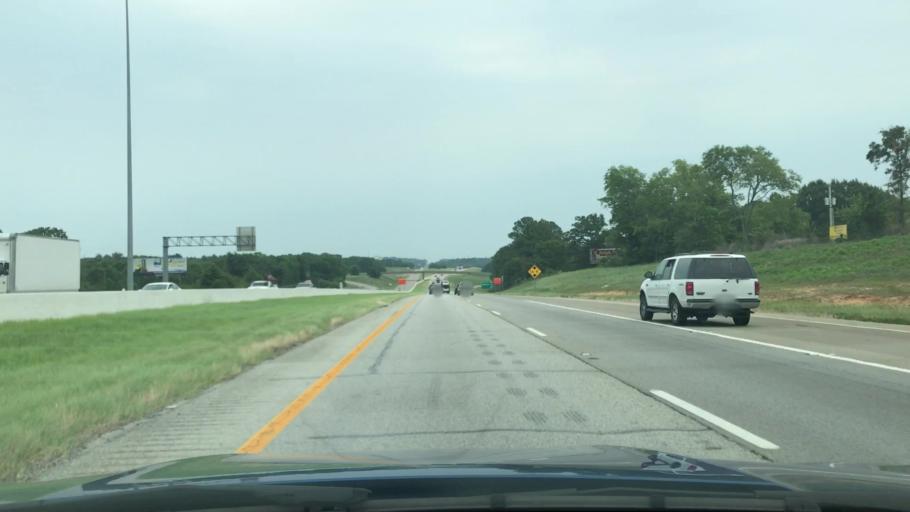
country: US
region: Texas
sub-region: Smith County
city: Hideaway
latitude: 32.4687
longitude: -95.4262
